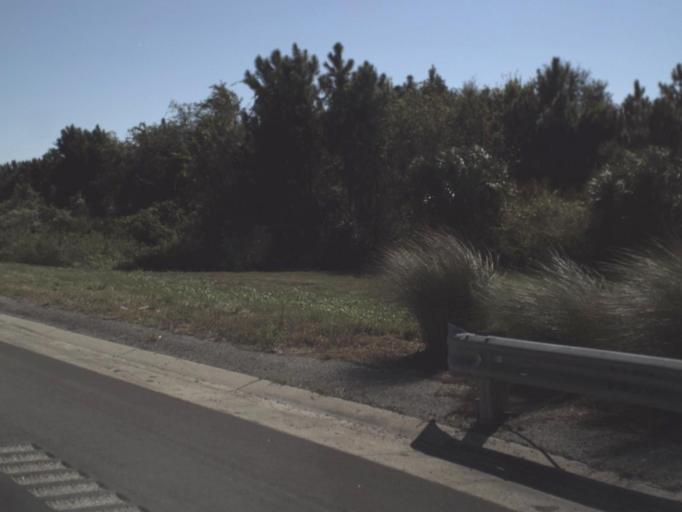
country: US
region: Florida
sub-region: Seminole County
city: Sanford
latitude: 28.7979
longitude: -81.3050
